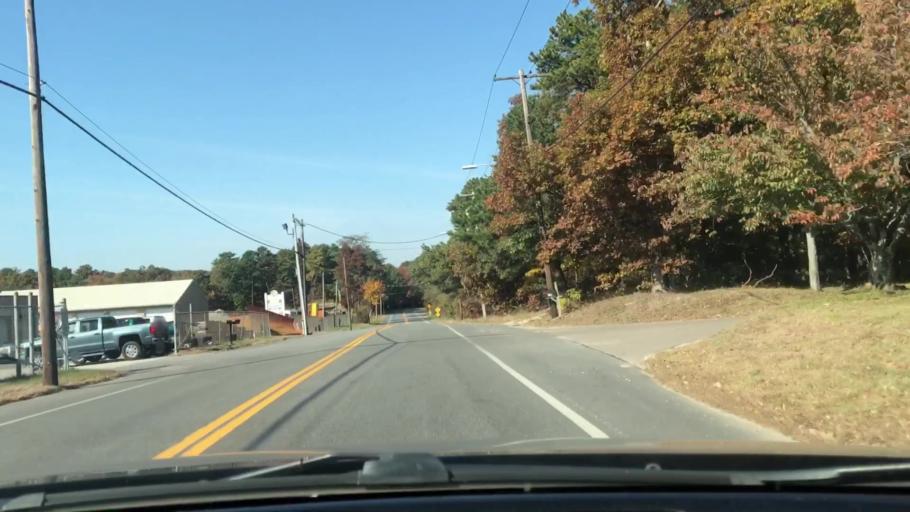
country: US
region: New York
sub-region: Suffolk County
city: Riverhead
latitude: 40.9293
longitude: -72.6883
